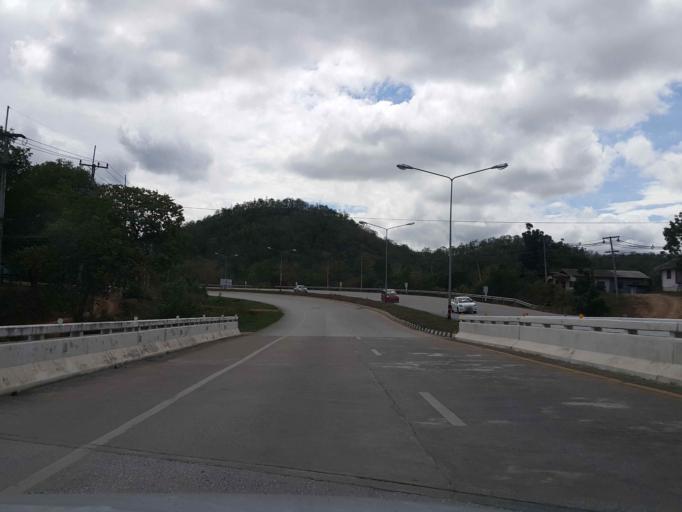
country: TH
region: Tak
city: Tak
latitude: 16.8191
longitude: 99.0696
